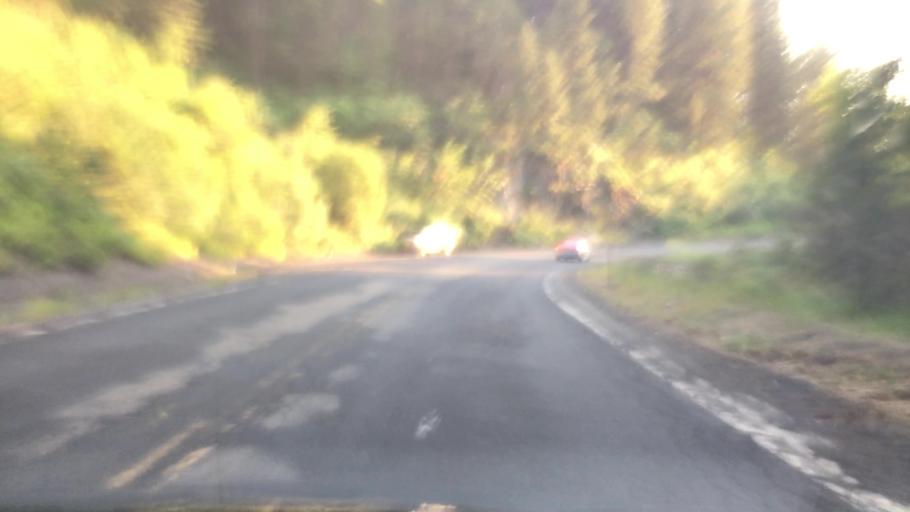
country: US
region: Idaho
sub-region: Valley County
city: McCall
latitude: 44.9596
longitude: -116.2083
